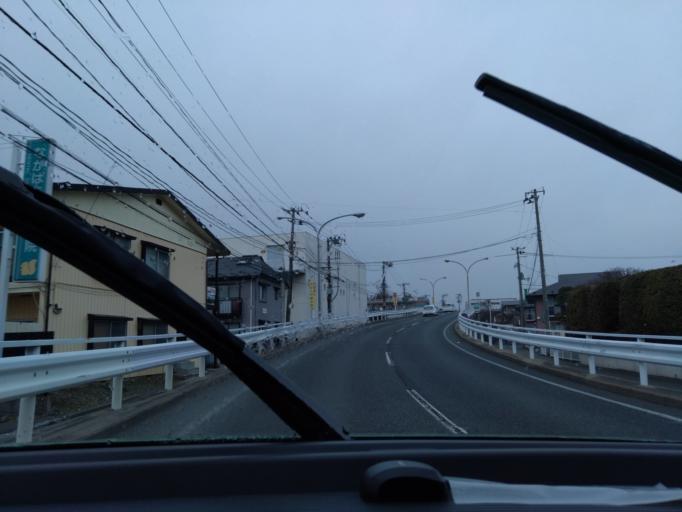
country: JP
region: Iwate
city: Morioka-shi
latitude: 39.7096
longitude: 141.1427
